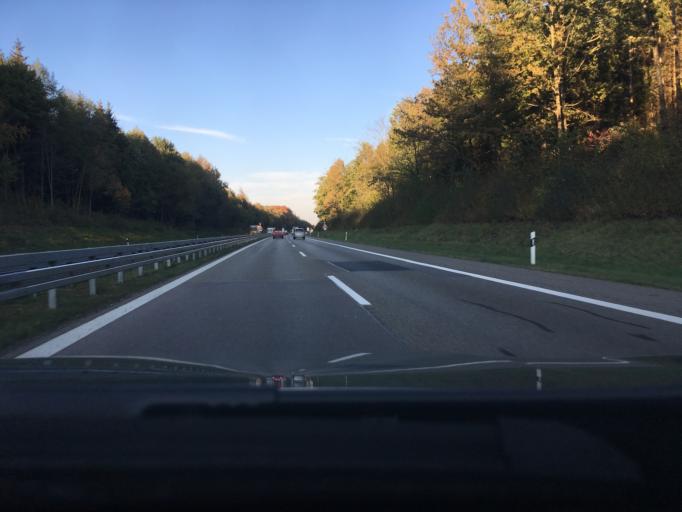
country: DE
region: Bavaria
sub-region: Swabia
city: Buxheim
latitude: 47.9797
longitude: 10.1245
